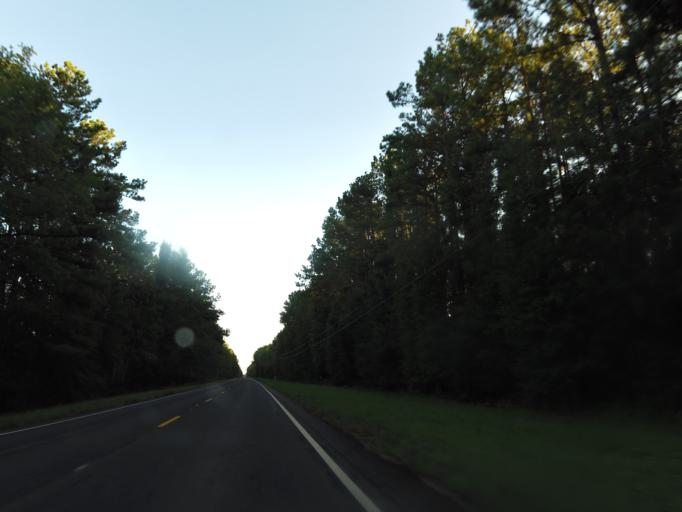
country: US
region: Georgia
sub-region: Camden County
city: Woodbine
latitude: 31.0647
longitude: -81.7286
